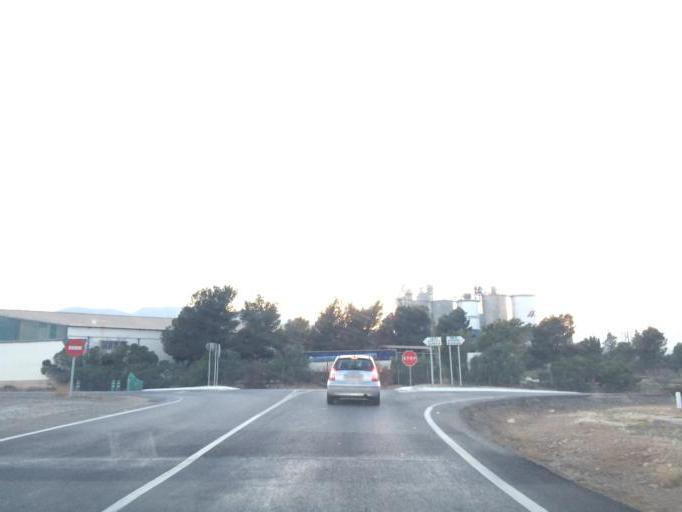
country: ES
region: Andalusia
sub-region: Provincia de Almeria
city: Rioja
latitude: 36.9357
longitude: -2.4719
